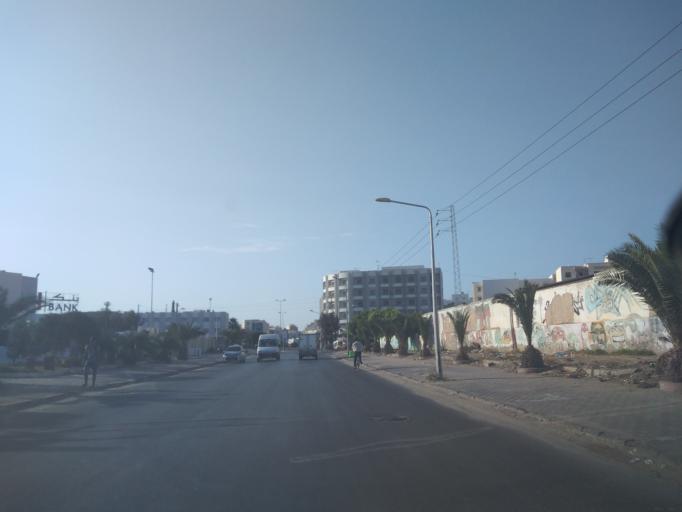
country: TN
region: Safaqis
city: Sfax
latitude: 34.7279
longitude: 10.7546
